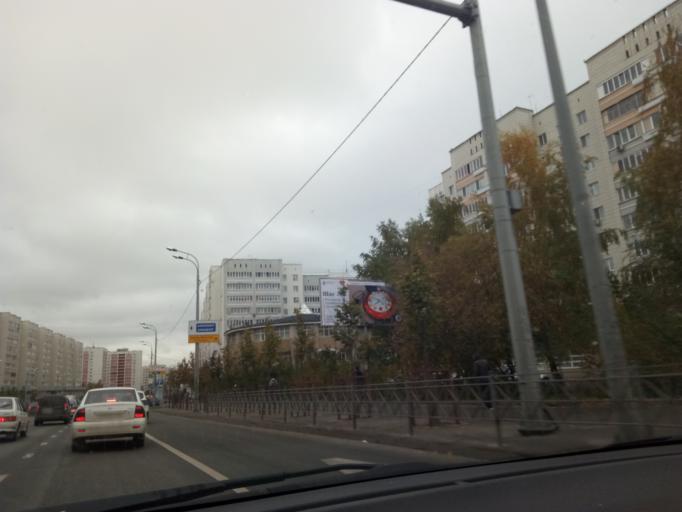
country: RU
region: Tatarstan
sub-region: Gorod Kazan'
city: Kazan
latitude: 55.7877
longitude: 49.1514
